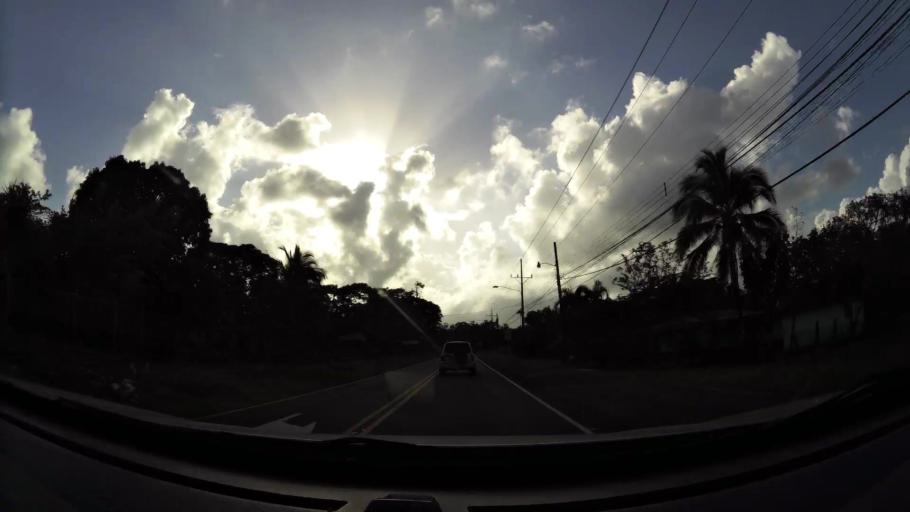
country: CR
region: Limon
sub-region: Canton de Siquirres
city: Siquirres
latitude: 10.0961
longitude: -83.5336
